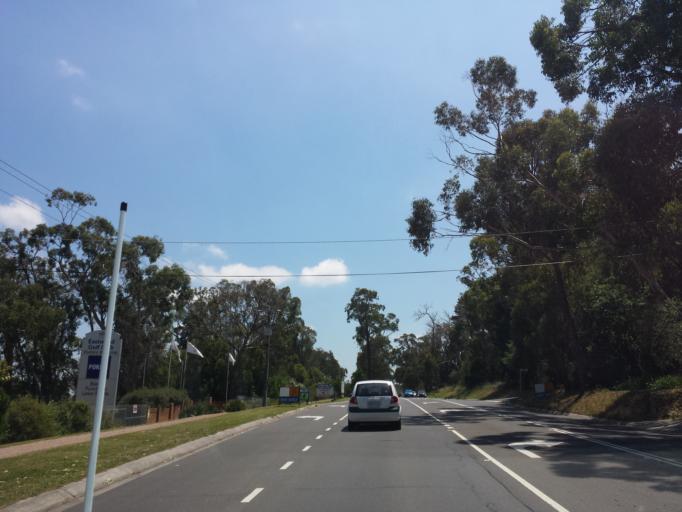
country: AU
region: Victoria
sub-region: Knox
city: The Basin
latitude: -37.8361
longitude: 145.3187
